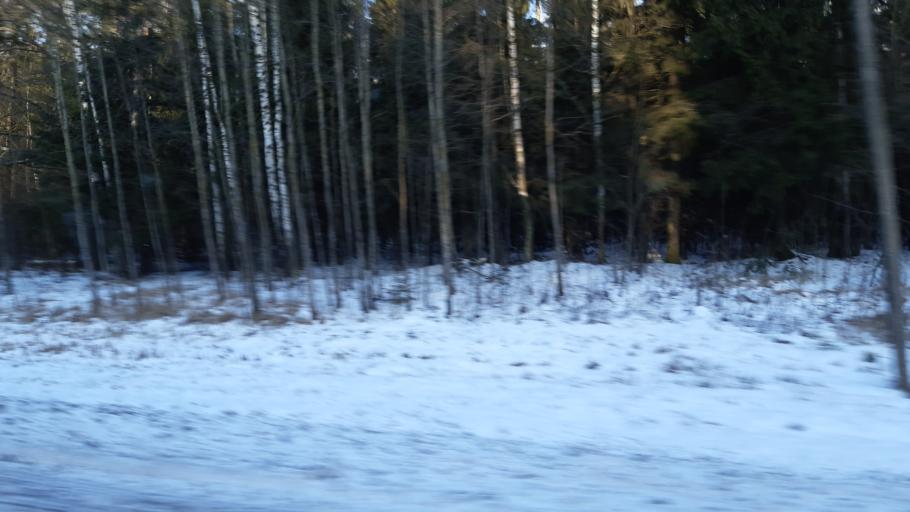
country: RU
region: Vladimir
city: Arsaki
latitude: 56.2928
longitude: 38.3757
